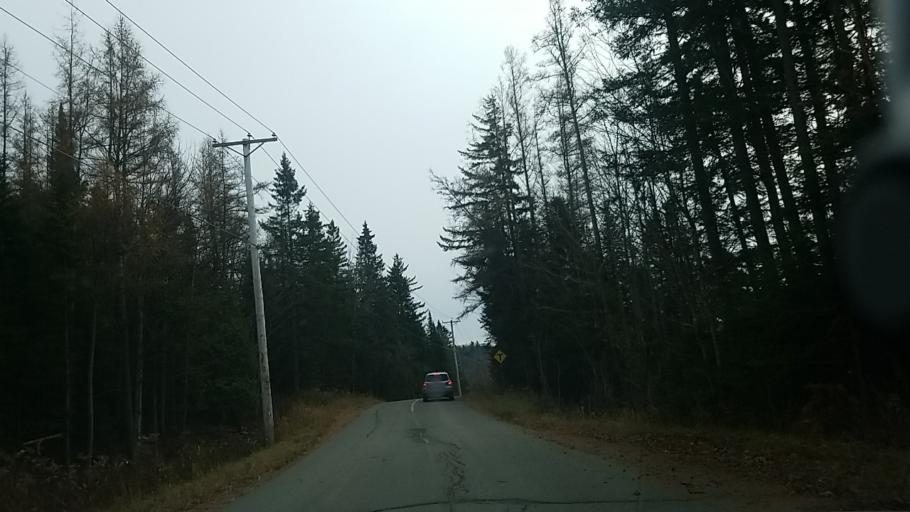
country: CA
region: Quebec
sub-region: Laurentides
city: Saint-Sauveur
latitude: 45.8186
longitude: -74.2489
